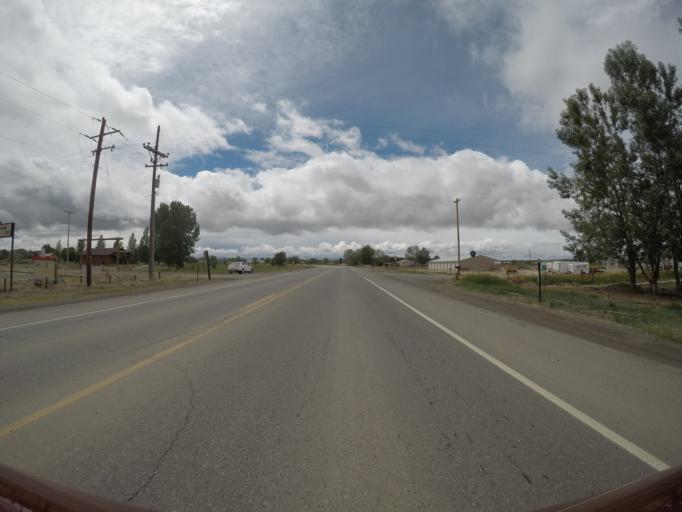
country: US
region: Wyoming
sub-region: Big Horn County
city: Lovell
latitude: 44.8404
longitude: -108.3725
